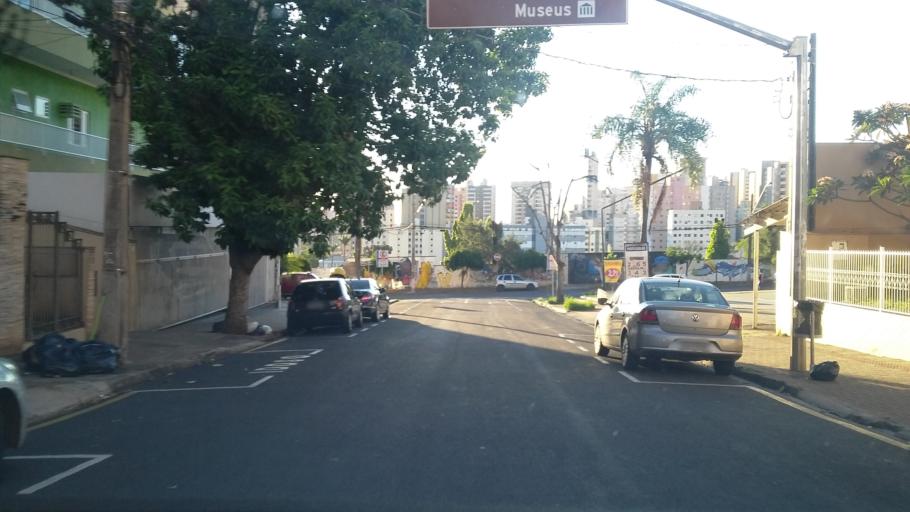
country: BR
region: Parana
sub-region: Londrina
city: Londrina
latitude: -23.3187
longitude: -51.1582
